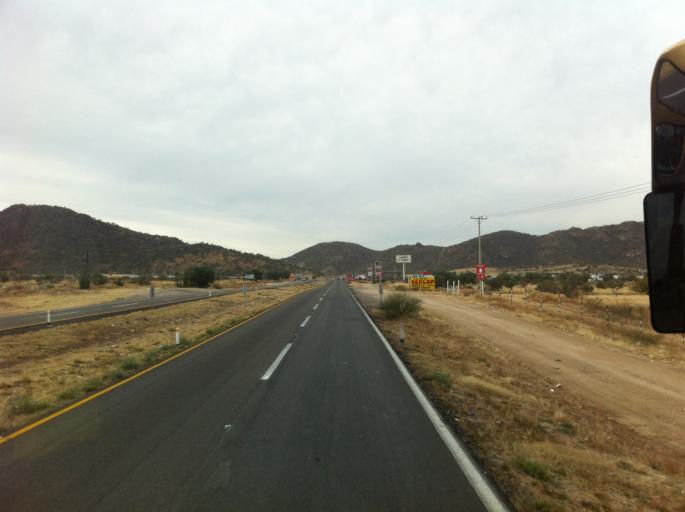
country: MX
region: Sonora
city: Hermosillo
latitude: 29.0037
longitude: -110.9671
